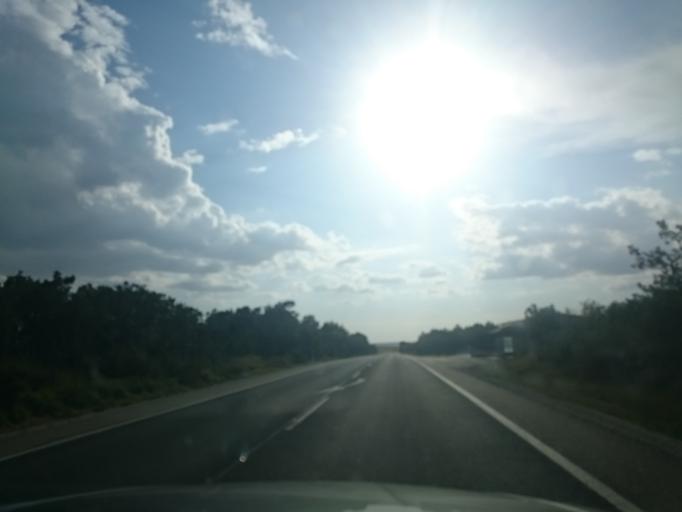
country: ES
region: Castille and Leon
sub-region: Provincia de Burgos
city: Arlanzon
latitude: 42.3509
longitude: -3.4295
